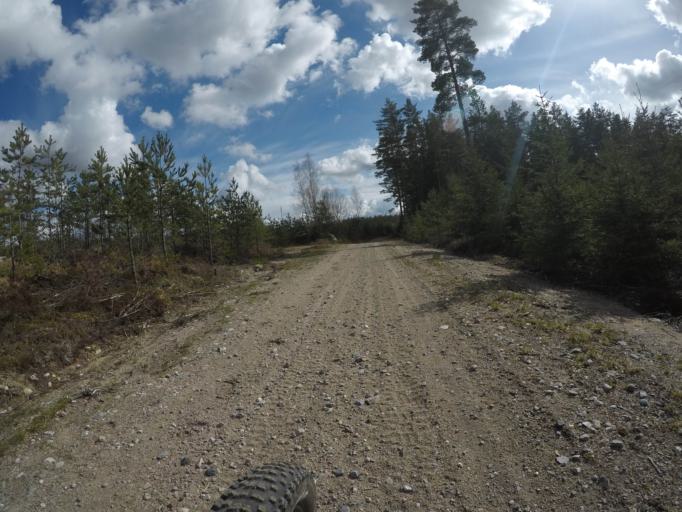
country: SE
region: Vaestmanland
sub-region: Kungsors Kommun
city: Kungsoer
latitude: 59.3466
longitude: 16.1081
